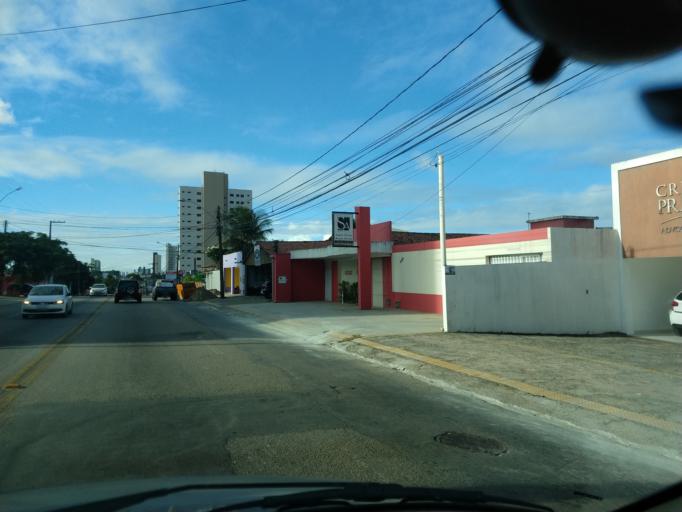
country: BR
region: Rio Grande do Norte
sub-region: Natal
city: Natal
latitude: -5.8284
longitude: -35.2218
